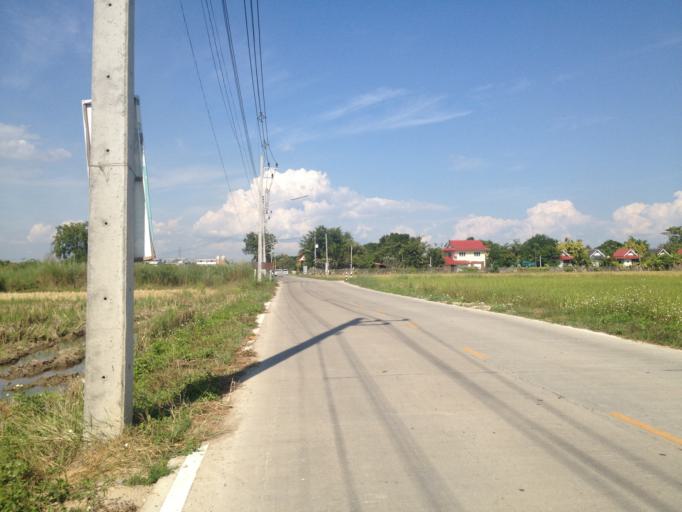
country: TH
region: Chiang Mai
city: Hang Dong
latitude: 18.7121
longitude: 98.9677
